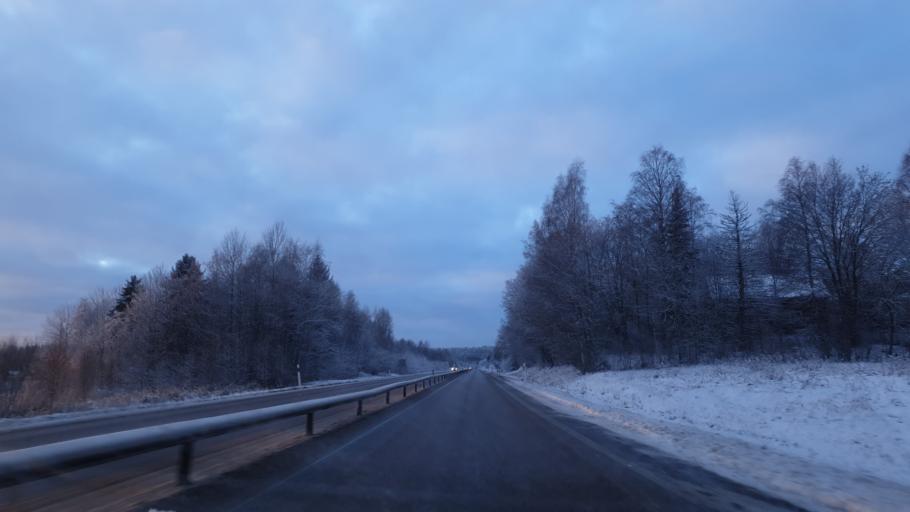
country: SE
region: Vaesternorrland
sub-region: OErnskoeldsviks Kommun
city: Husum
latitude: 63.3465
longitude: 19.1366
